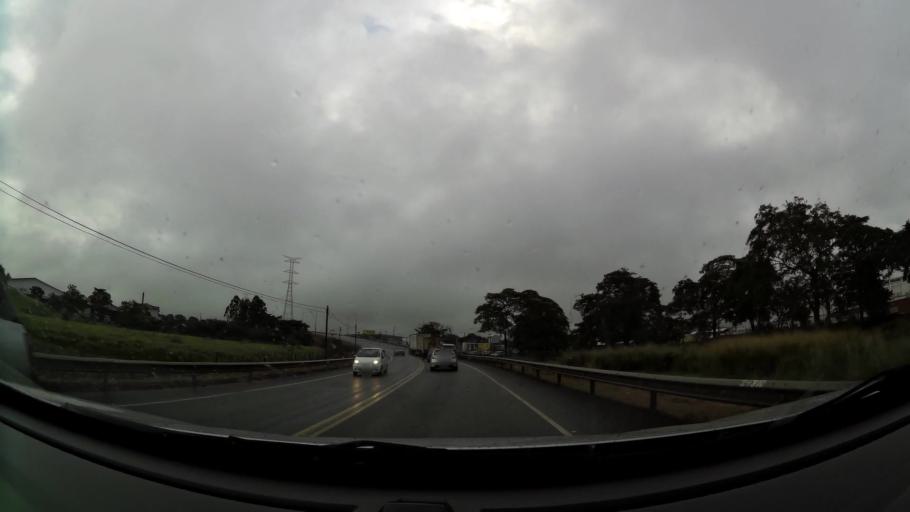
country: CR
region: Alajuela
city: Carrillos
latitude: 9.9808
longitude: -84.2691
